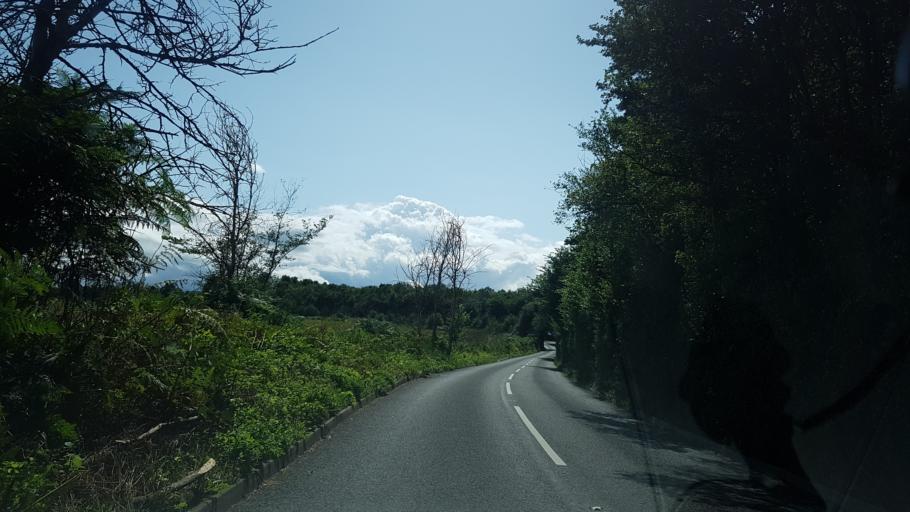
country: GB
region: England
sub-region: Surrey
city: West Byfleet
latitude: 51.3205
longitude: -0.5100
